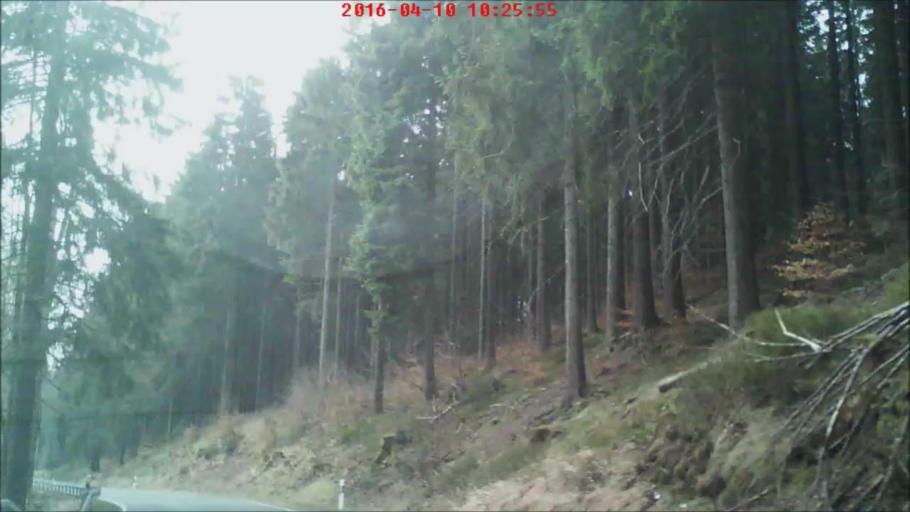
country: DE
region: Thuringia
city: Stutzerbach
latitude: 50.6431
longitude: 10.8762
